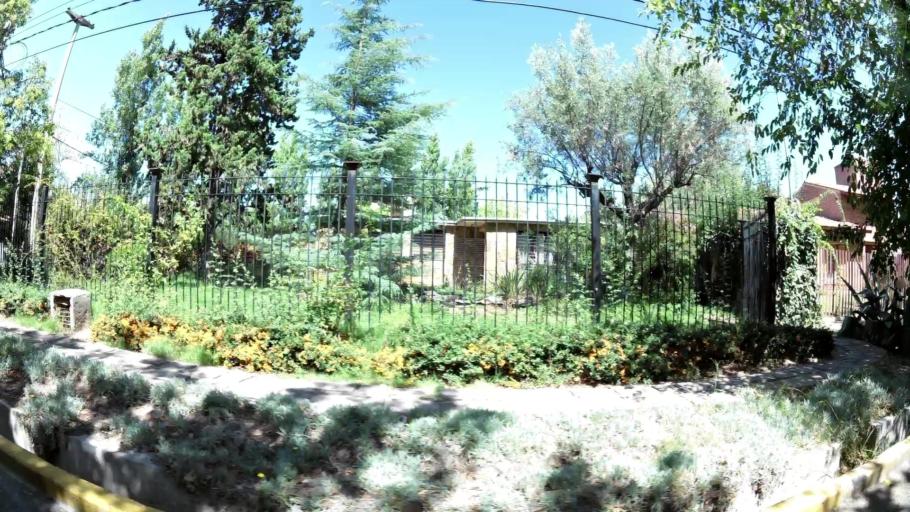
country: AR
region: Mendoza
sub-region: Departamento de Godoy Cruz
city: Godoy Cruz
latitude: -32.9616
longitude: -68.8620
